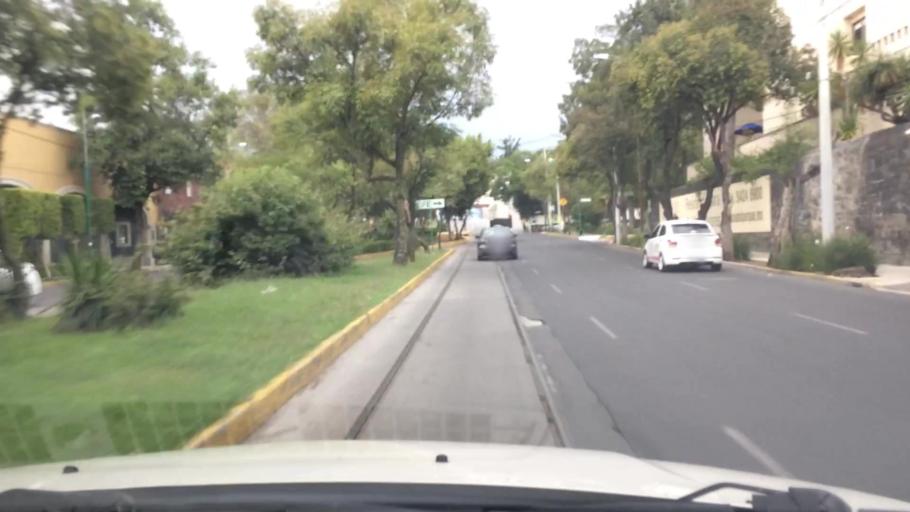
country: MX
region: Mexico City
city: Tlalpan
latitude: 19.2934
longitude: -99.1647
